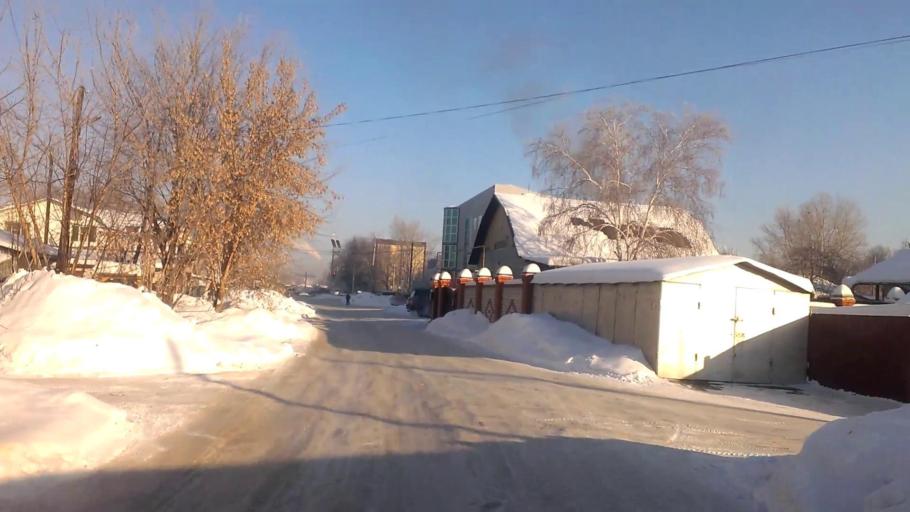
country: RU
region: Altai Krai
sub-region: Gorod Barnaulskiy
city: Barnaul
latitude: 53.3479
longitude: 83.7270
